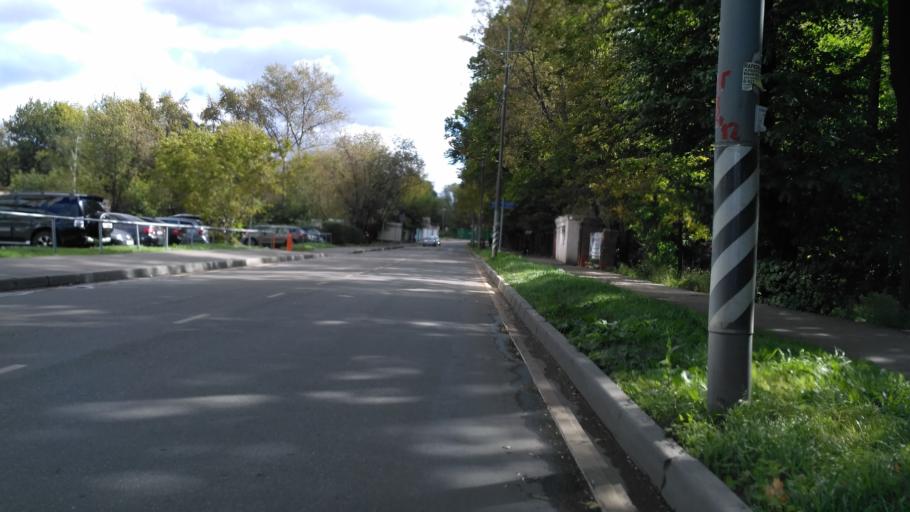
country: RU
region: Moscow
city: Sokol'niki
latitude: 55.8101
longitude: 37.6555
